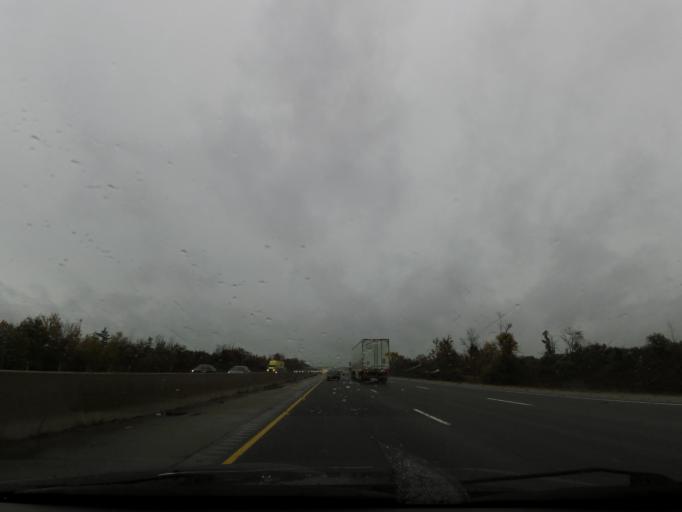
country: CA
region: Ontario
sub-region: Wellington County
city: Guelph
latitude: 43.4399
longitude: -80.2184
